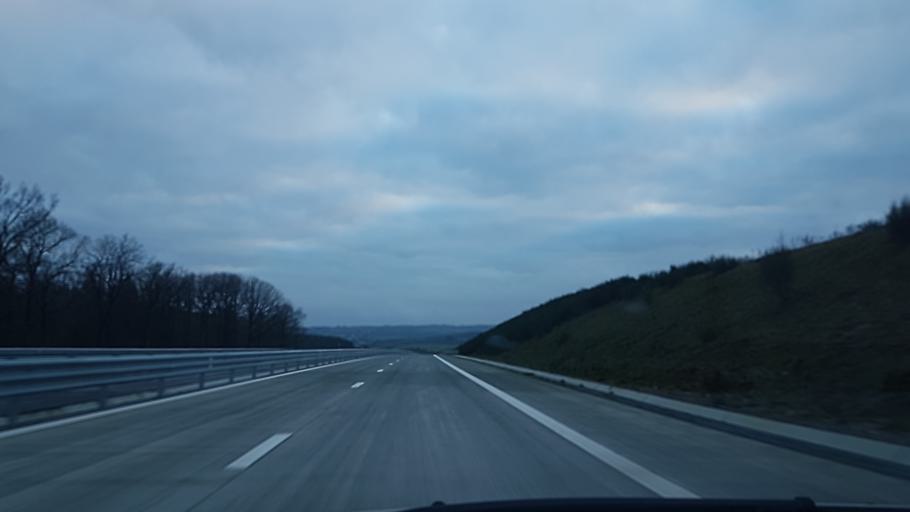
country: FR
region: Champagne-Ardenne
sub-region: Departement des Ardennes
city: Rocroi
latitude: 49.9908
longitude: 4.5419
